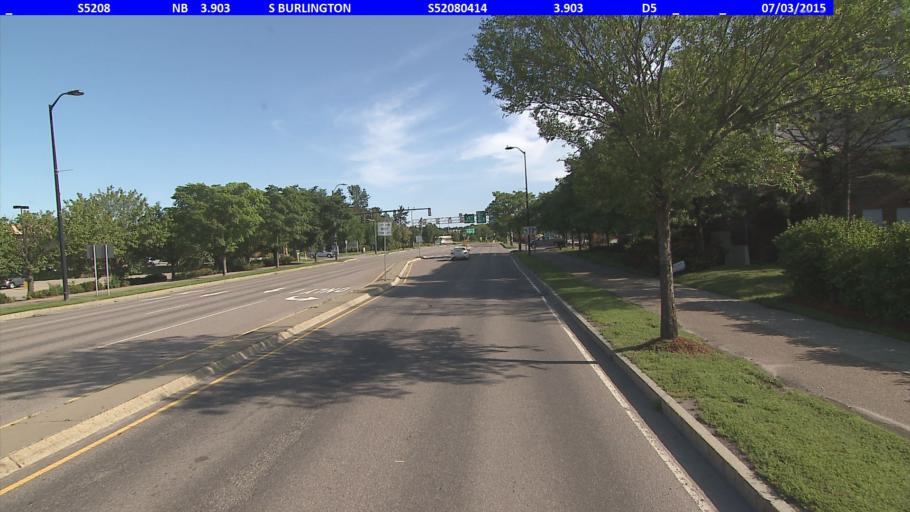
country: US
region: Vermont
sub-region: Chittenden County
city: South Burlington
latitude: 44.4663
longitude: -73.1811
